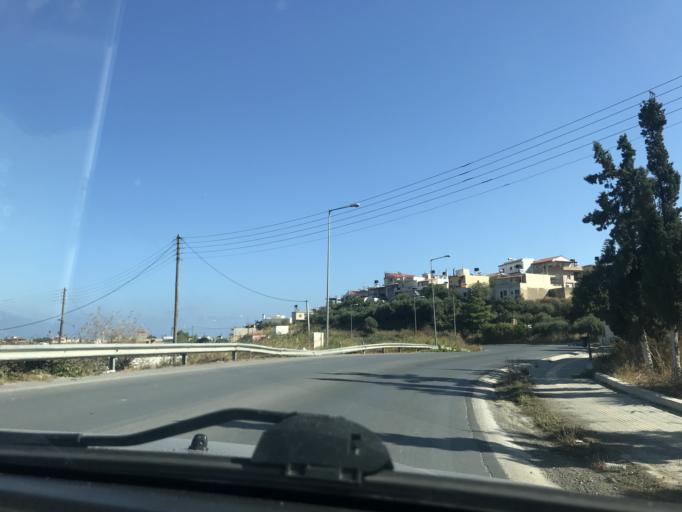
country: GR
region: Crete
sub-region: Nomos Irakleiou
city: Gazi
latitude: 35.3256
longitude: 25.0626
